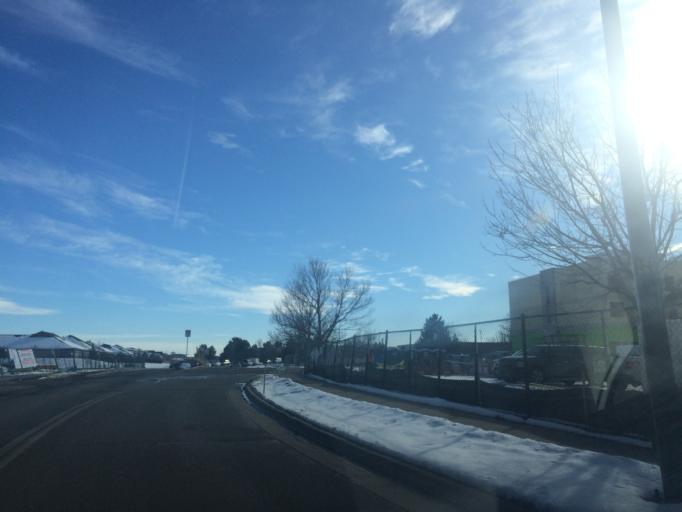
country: US
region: Colorado
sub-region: Boulder County
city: Lafayette
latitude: 39.9879
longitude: -105.0881
